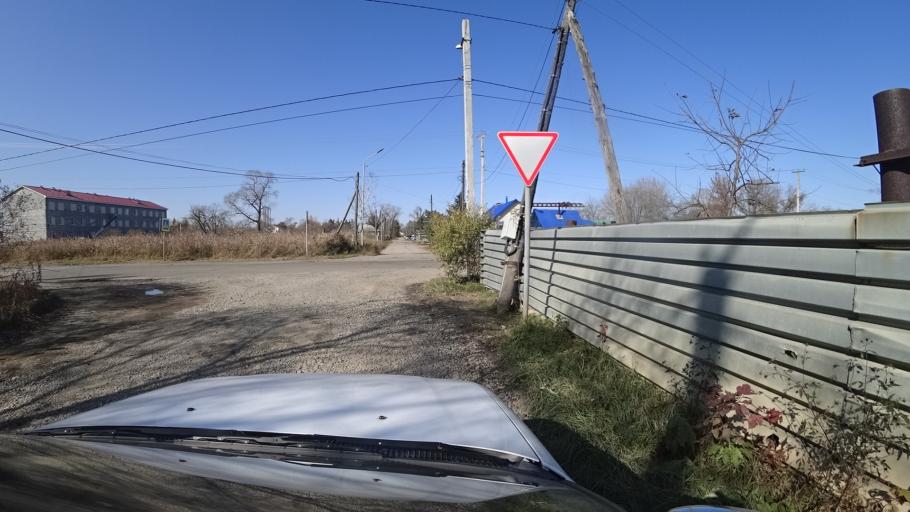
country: RU
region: Primorskiy
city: Dal'nerechensk
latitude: 45.9321
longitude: 133.7486
